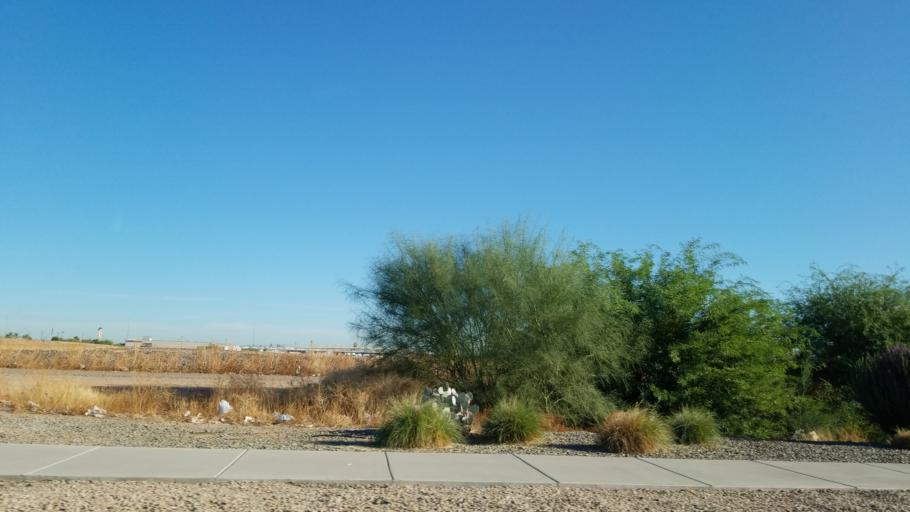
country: US
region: Arizona
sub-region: Maricopa County
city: Tolleson
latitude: 33.4503
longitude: -112.2704
